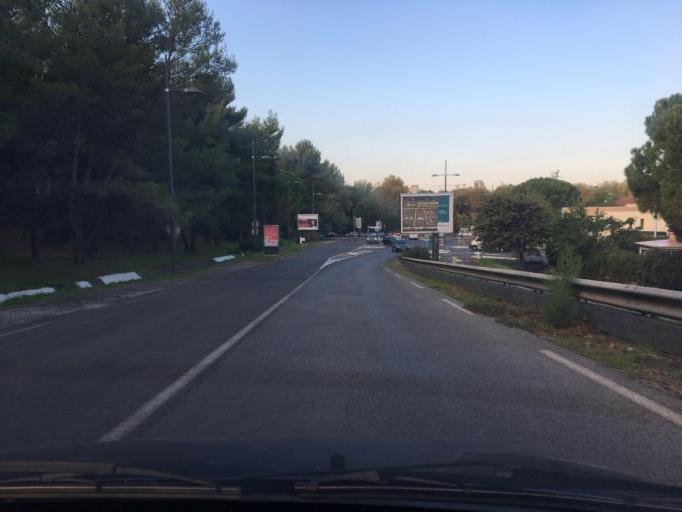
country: FR
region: Languedoc-Roussillon
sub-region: Departement de l'Herault
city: Castelnau-le-Lez
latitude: 43.6103
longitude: 3.9008
